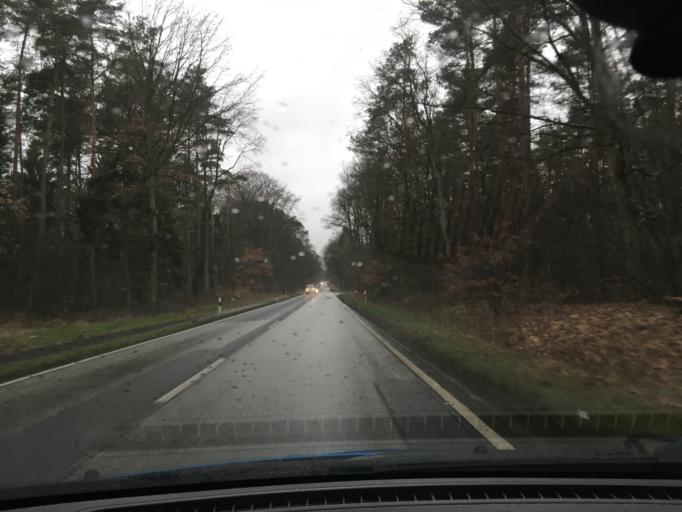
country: DE
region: Schleswig-Holstein
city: Schnakenbek
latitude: 53.3889
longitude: 10.4911
